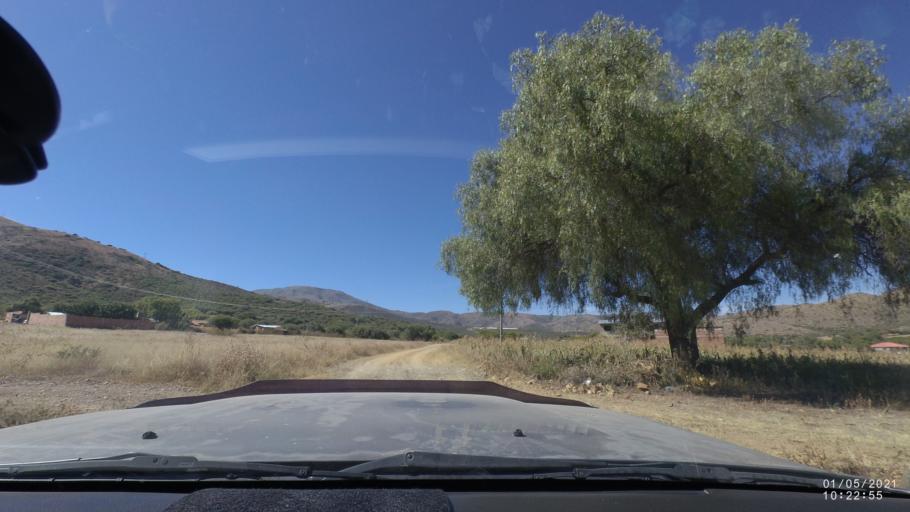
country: BO
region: Cochabamba
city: Capinota
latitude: -17.5700
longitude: -66.1979
